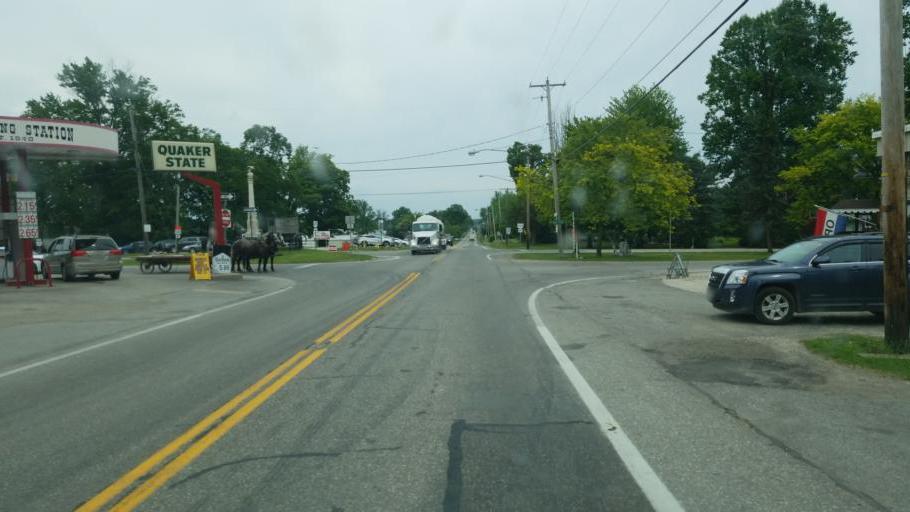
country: US
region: Ohio
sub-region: Ashtabula County
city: Orwell
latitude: 41.4583
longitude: -80.9555
